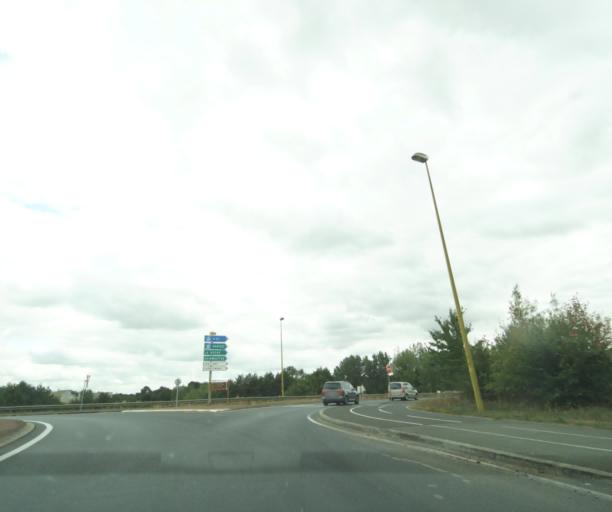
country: FR
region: Pays de la Loire
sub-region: Departement de la Vendee
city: Montaigu
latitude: 46.9650
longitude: -1.3080
